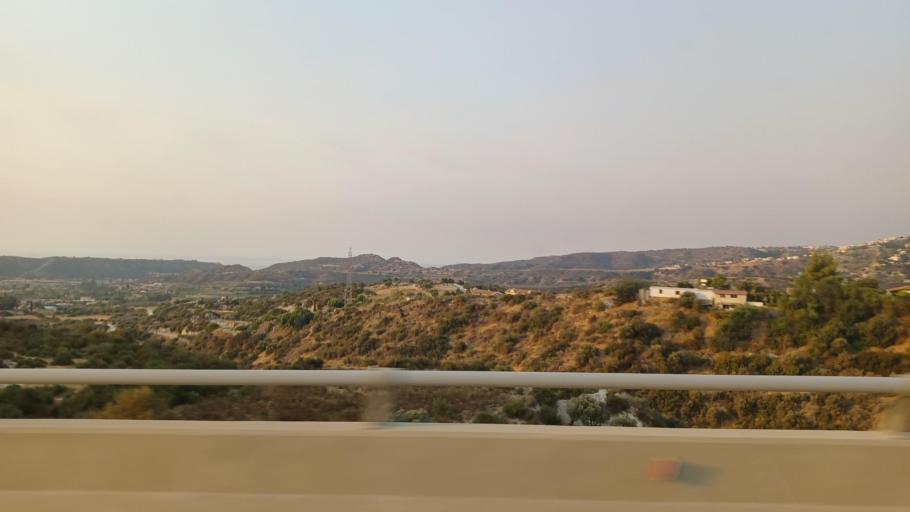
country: CY
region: Limassol
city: Pissouri
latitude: 34.6851
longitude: 32.7118
